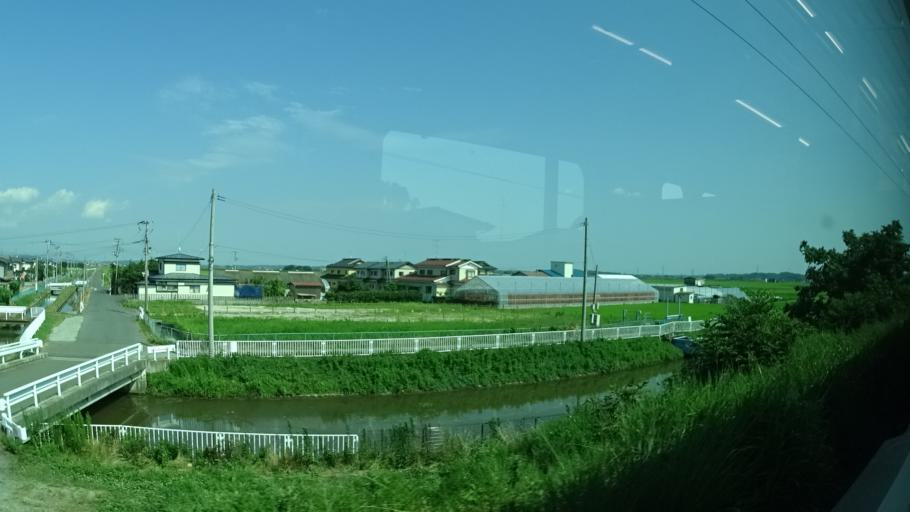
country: JP
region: Miyagi
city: Wakuya
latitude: 38.4725
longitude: 141.0978
